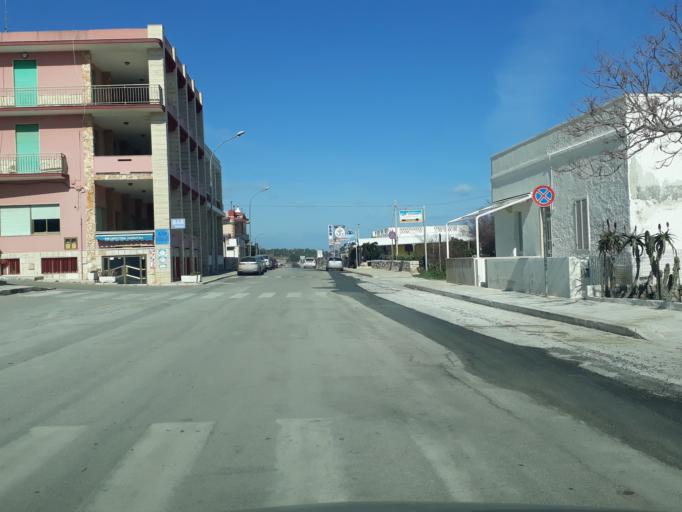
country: IT
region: Apulia
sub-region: Provincia di Bari
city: Monopoli
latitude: 40.9064
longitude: 17.3483
